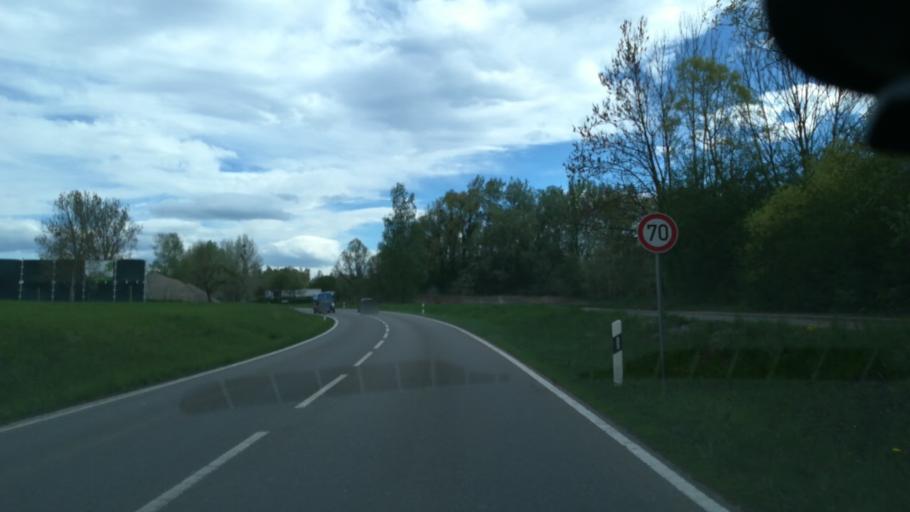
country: DE
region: Baden-Wuerttemberg
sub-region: Freiburg Region
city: Moos
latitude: 47.7493
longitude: 8.9231
